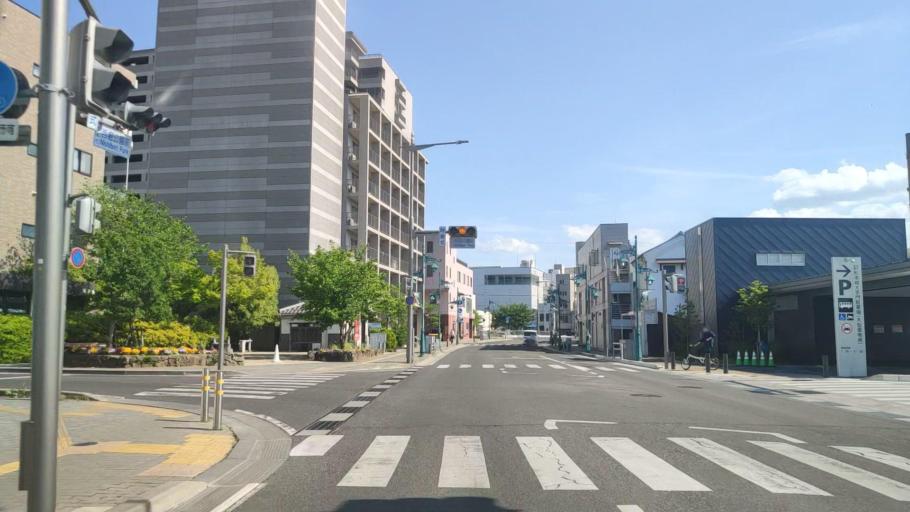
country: JP
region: Nagano
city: Matsumoto
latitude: 36.2352
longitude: 137.9674
